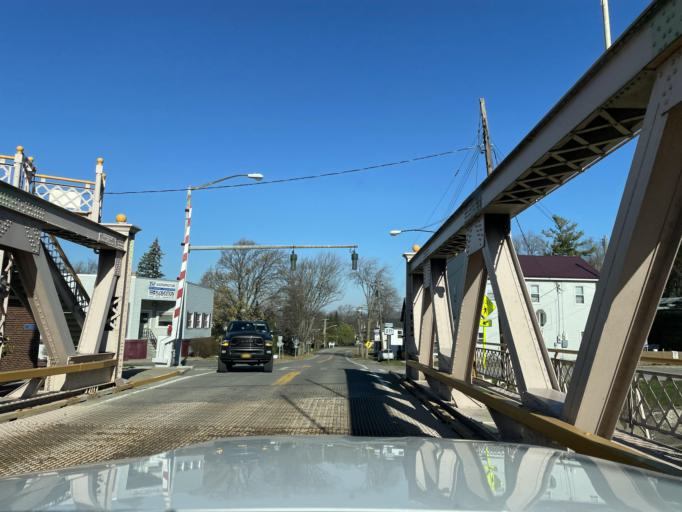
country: US
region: New York
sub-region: Niagara County
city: Middleport
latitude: 43.2129
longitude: -78.4765
